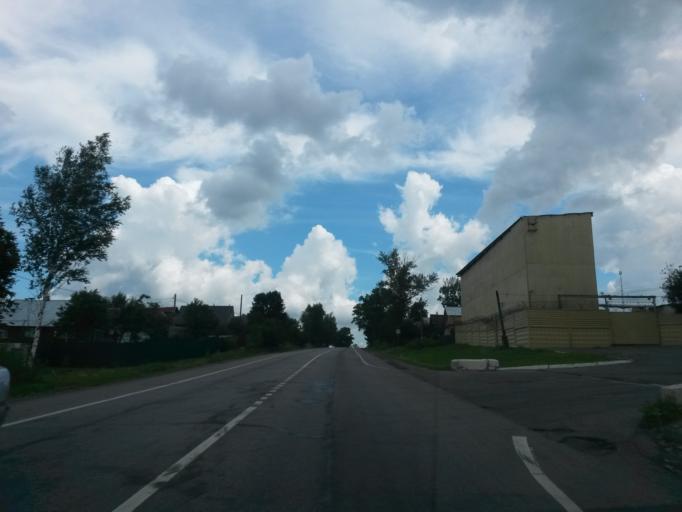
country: RU
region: Vladimir
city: Aleksandrov
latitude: 56.5969
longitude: 38.6223
